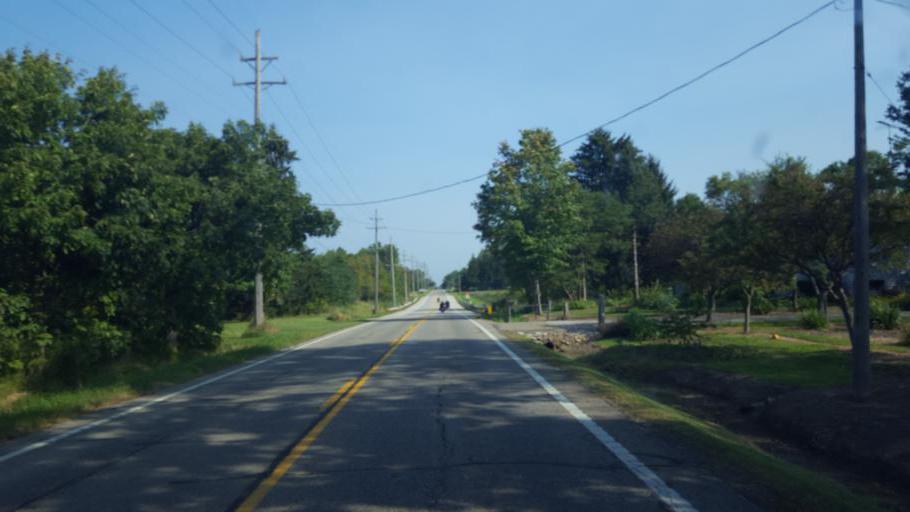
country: US
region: Ohio
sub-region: Ashtabula County
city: Orwell
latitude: 41.5736
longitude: -80.8651
